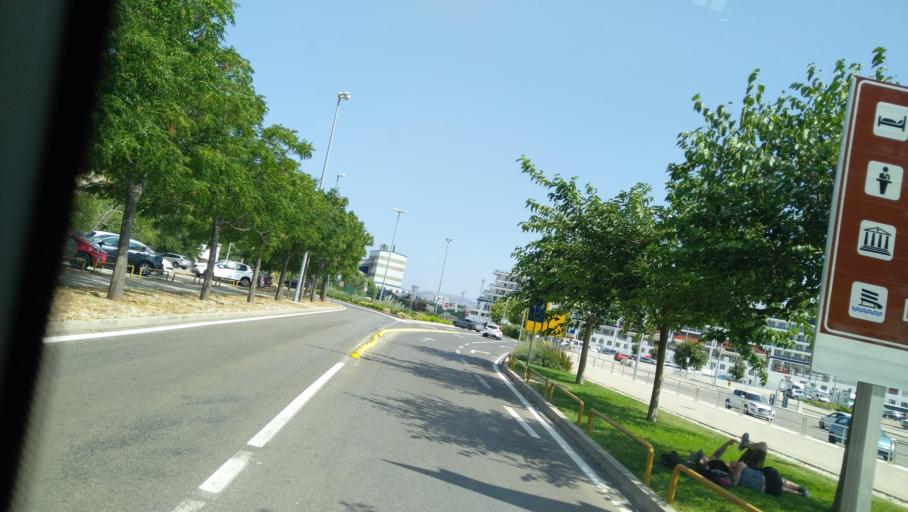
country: HR
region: Sibensko-Kniniska
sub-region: Grad Sibenik
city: Sibenik
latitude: 43.7310
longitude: 15.8946
